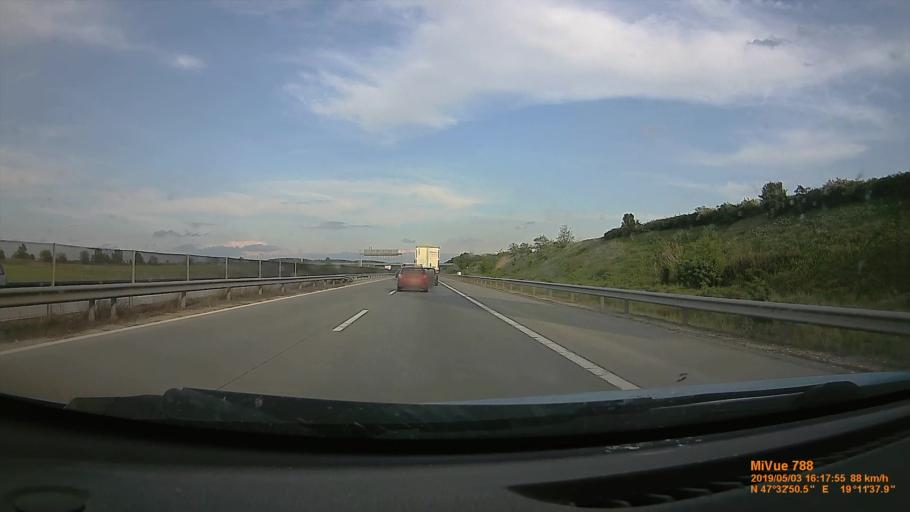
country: HU
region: Pest
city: Csomor
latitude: 47.5479
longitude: 19.1944
